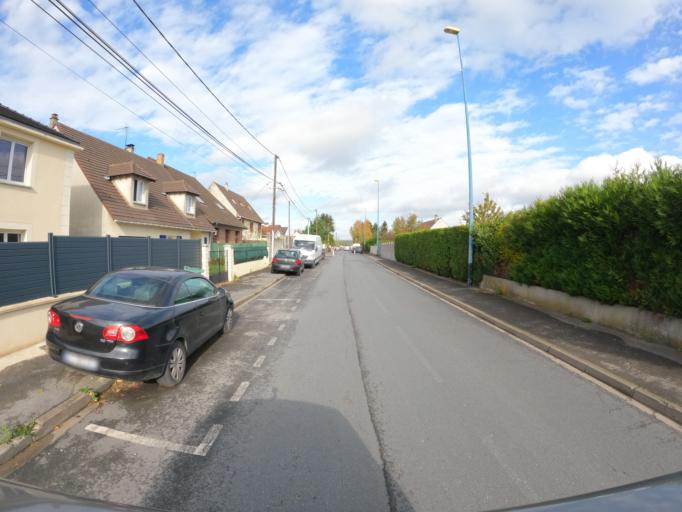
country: FR
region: Ile-de-France
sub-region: Departement de Seine-et-Marne
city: Chelles
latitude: 48.8906
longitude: 2.6038
